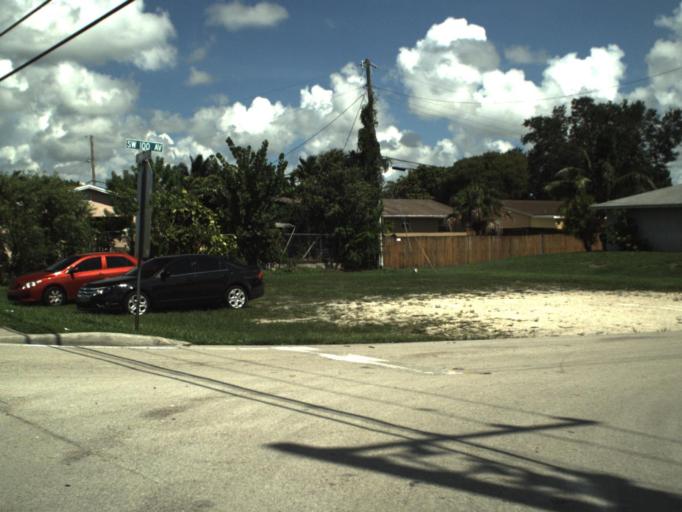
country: US
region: Florida
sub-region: Broward County
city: Miramar
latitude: 25.9937
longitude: -80.2778
